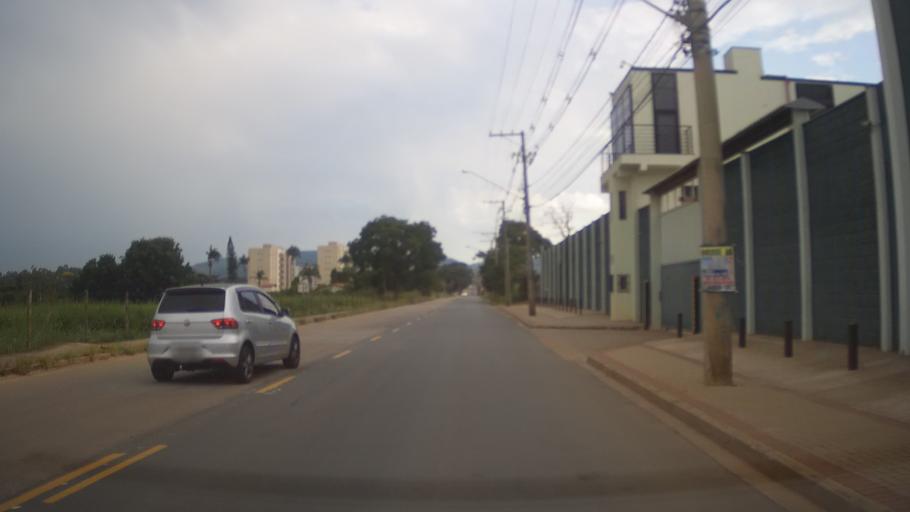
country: BR
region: Sao Paulo
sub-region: Itupeva
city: Itupeva
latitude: -23.1698
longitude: -47.0034
